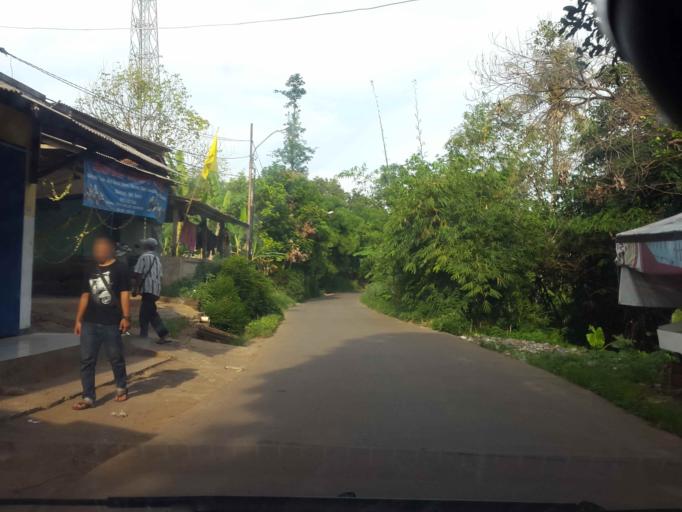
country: ID
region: Banten
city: South Tangerang
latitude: -6.2814
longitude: 106.6873
